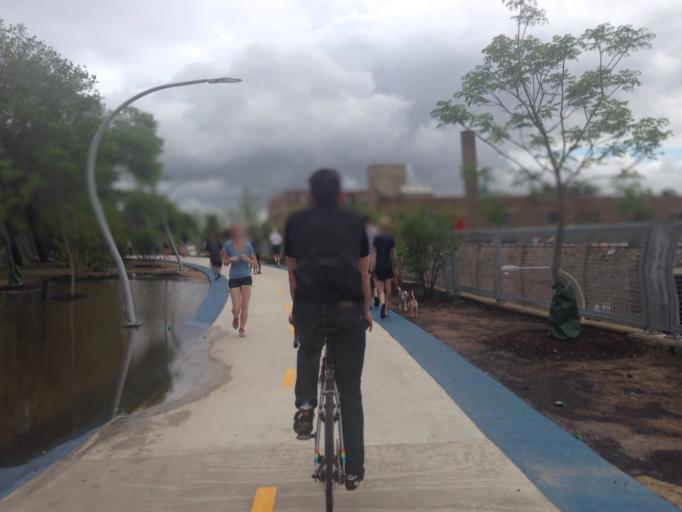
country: US
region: Illinois
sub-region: Cook County
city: Oak Park
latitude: 41.9137
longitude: -87.7128
